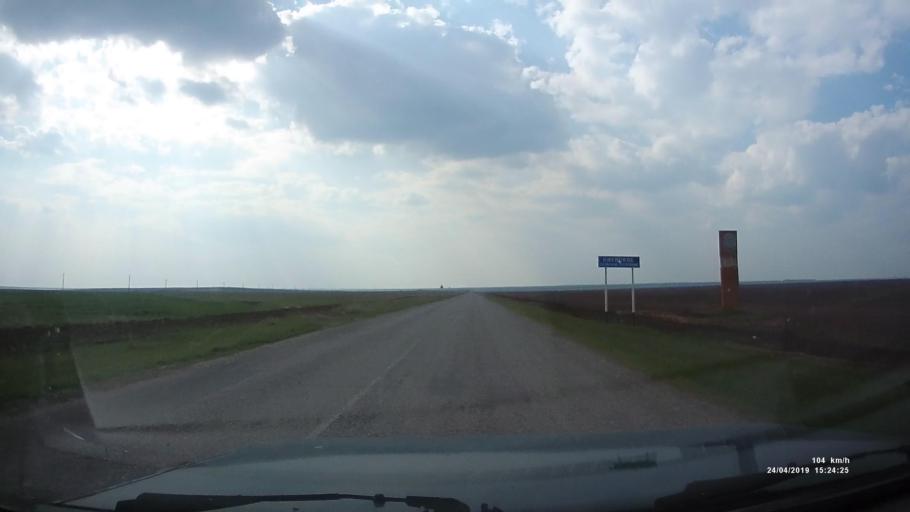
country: RU
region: Rostov
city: Remontnoye
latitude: 46.5478
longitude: 43.0688
